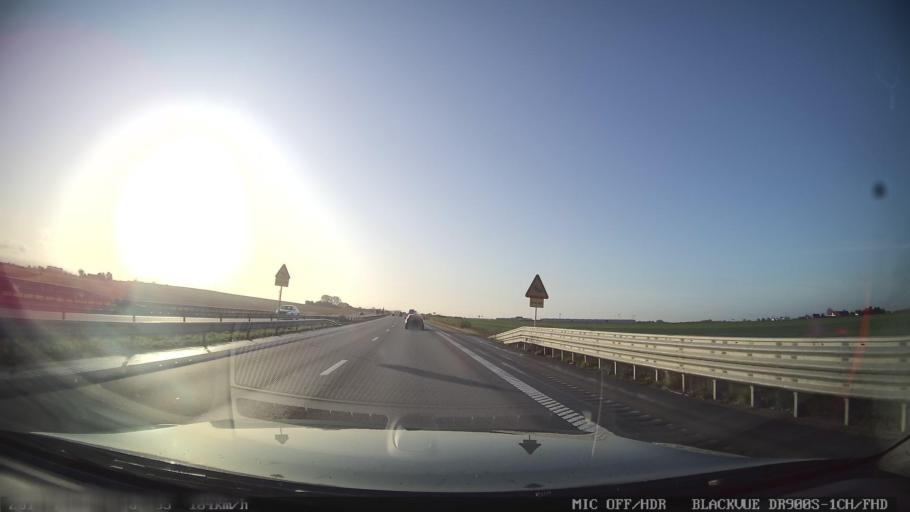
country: SE
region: Skane
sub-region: Landskrona
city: Landskrona
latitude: 55.8908
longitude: 12.8710
